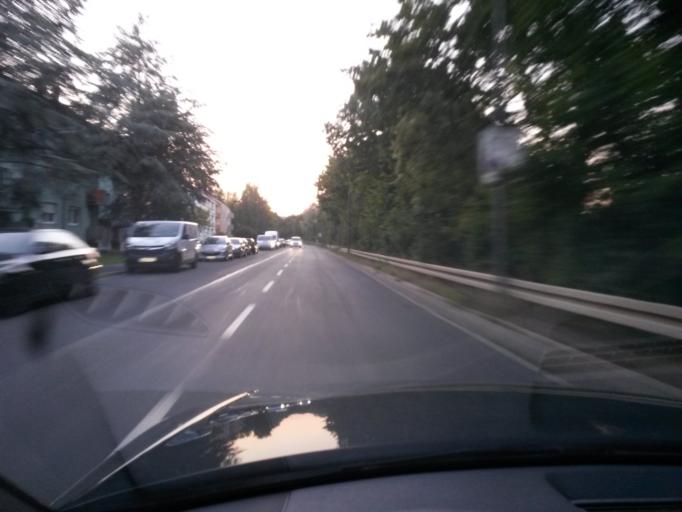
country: DE
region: Bavaria
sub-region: Regierungsbezirk Unterfranken
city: Randersacker
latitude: 49.7626
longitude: 9.9607
